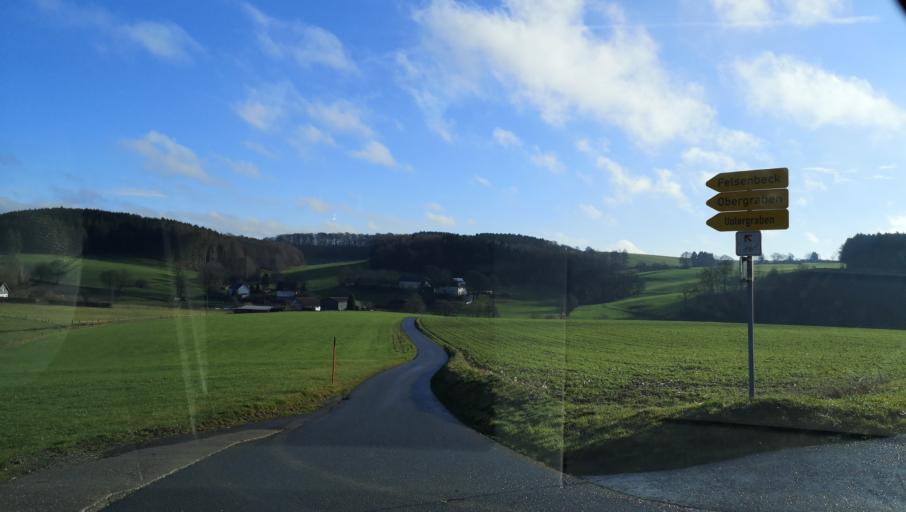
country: DE
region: North Rhine-Westphalia
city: Radevormwald
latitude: 51.1852
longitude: 7.4157
